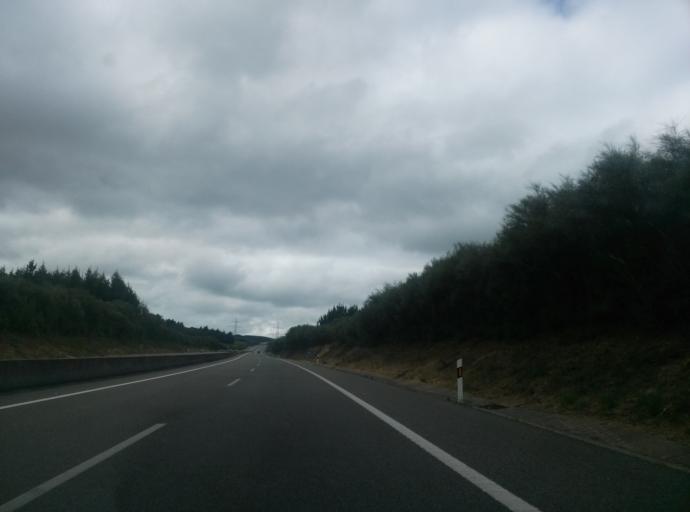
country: ES
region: Galicia
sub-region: Provincia de Lugo
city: Vilalba
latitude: 43.3257
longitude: -7.6944
